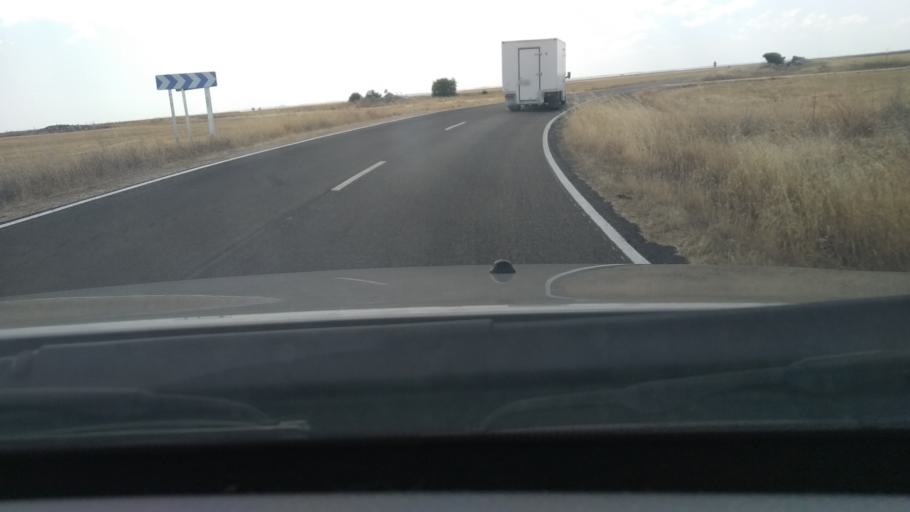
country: ES
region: Castille and Leon
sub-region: Provincia de Burgos
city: Iglesiarrubia
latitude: 41.9468
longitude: -3.8411
